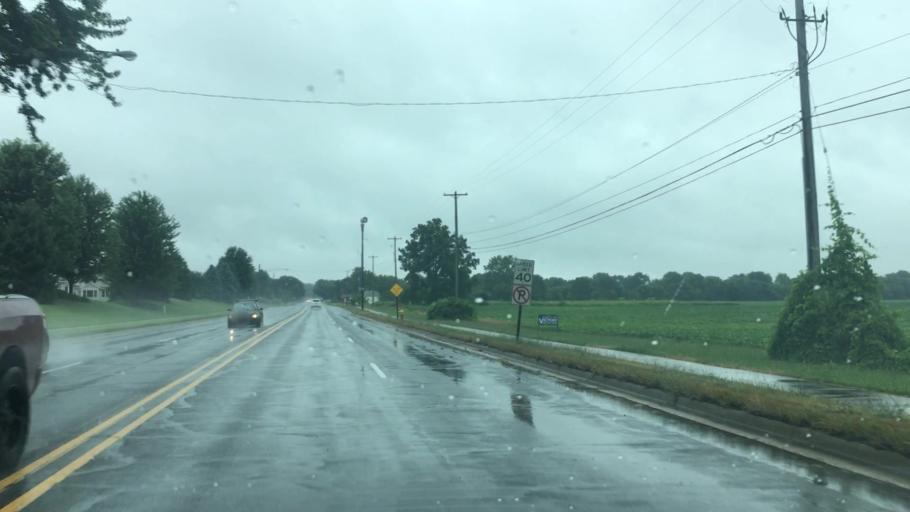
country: US
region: Michigan
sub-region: Ottawa County
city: Hudsonville
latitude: 42.8767
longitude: -85.8577
